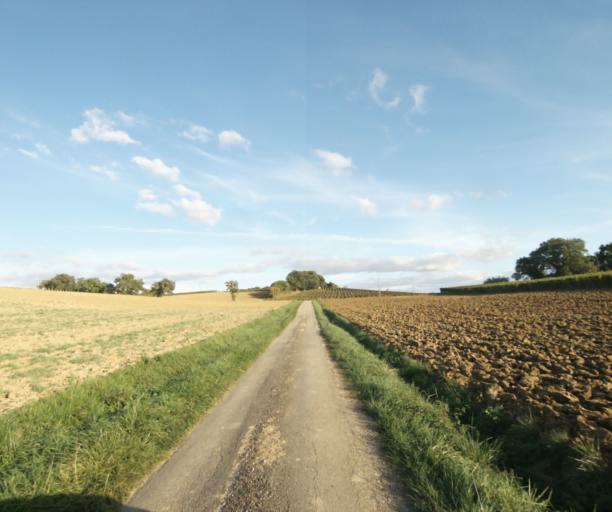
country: FR
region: Midi-Pyrenees
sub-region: Departement du Gers
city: Gondrin
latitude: 43.8750
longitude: 0.3085
